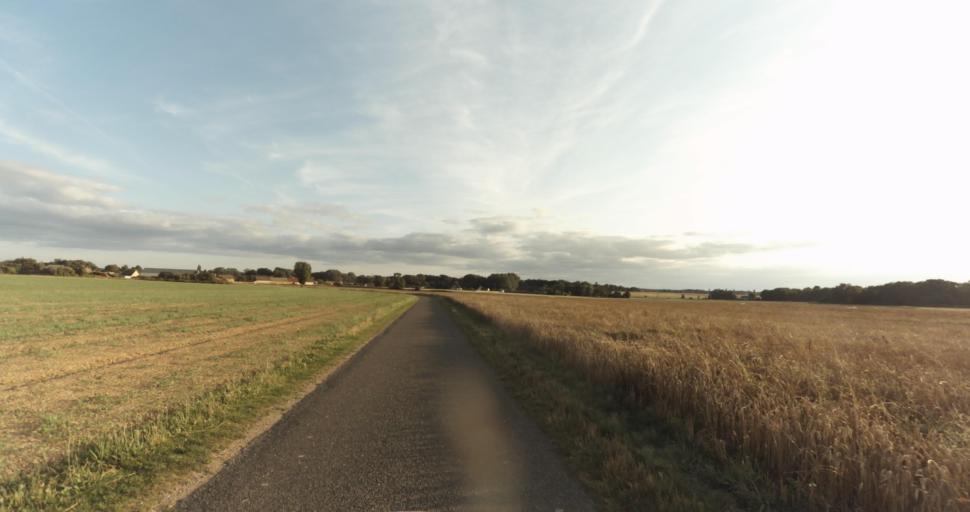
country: FR
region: Haute-Normandie
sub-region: Departement de l'Eure
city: Saint-Germain-sur-Avre
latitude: 48.8271
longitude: 1.2654
